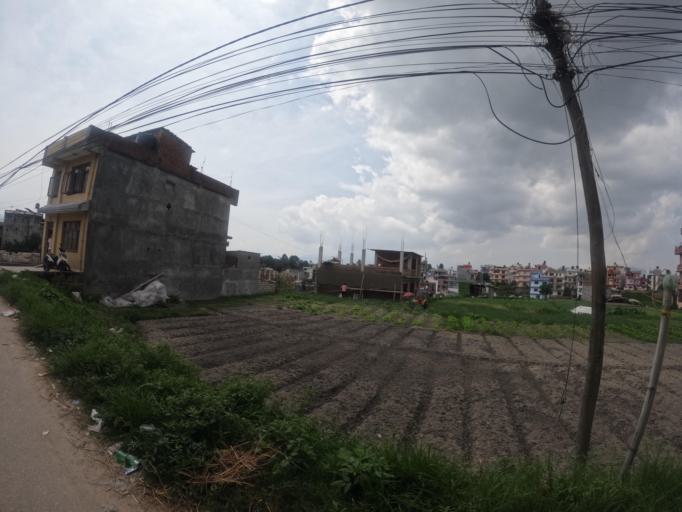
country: NP
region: Central Region
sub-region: Bagmati Zone
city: Bhaktapur
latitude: 27.6873
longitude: 85.3856
